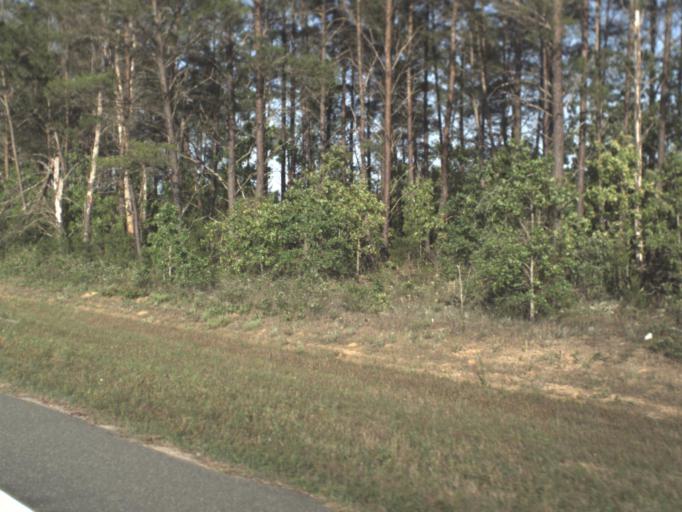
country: US
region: Florida
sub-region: Gadsden County
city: Gretna
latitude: 30.4560
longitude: -84.7475
